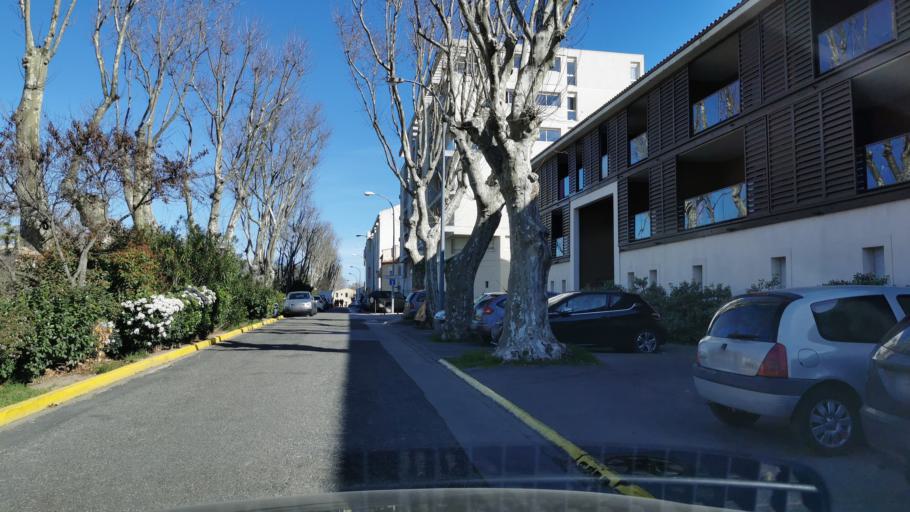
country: FR
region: Languedoc-Roussillon
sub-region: Departement de l'Aude
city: Narbonne
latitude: 43.1898
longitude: 2.9982
